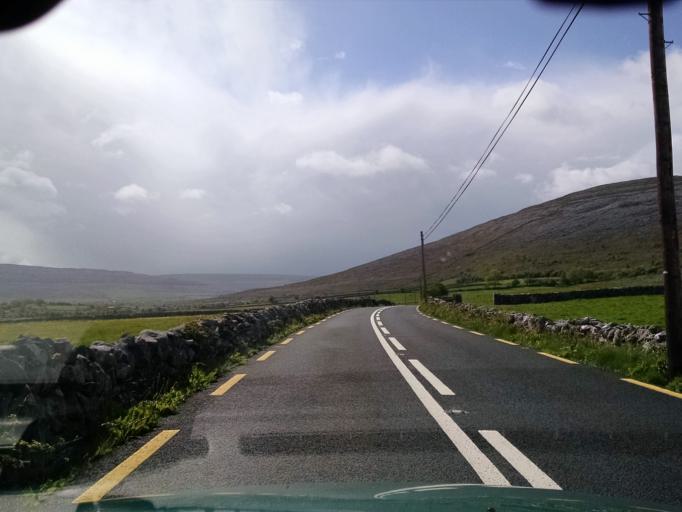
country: IE
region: Connaught
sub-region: County Galway
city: Bearna
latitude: 53.1332
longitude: -9.0975
